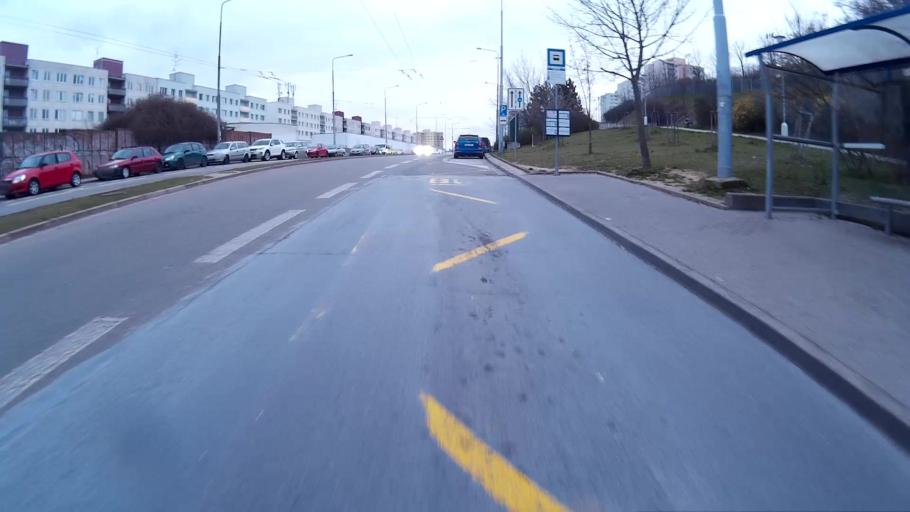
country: CZ
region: South Moravian
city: Ostopovice
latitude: 49.1766
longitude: 16.5583
